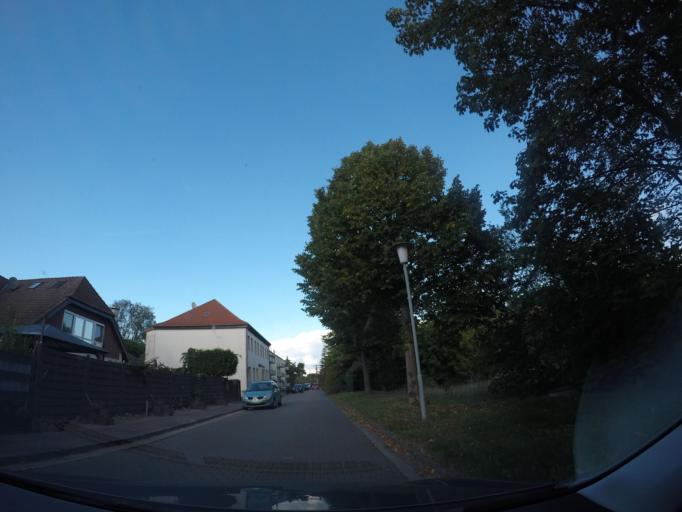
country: DE
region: Saxony-Anhalt
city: Kusey
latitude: 52.5812
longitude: 11.0977
